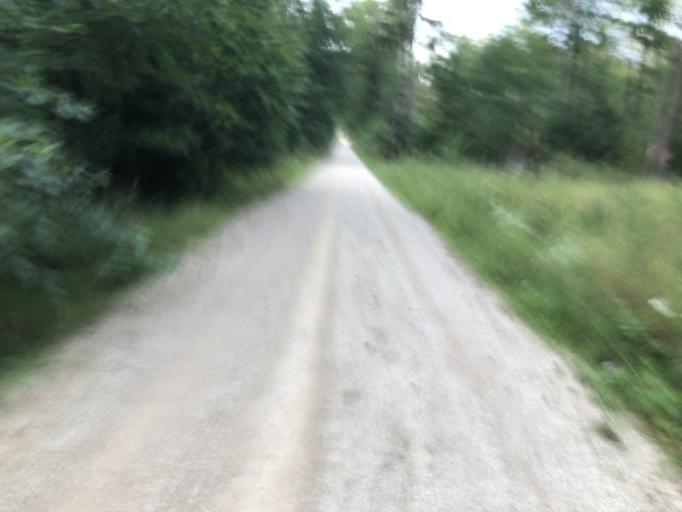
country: DE
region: Bavaria
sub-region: Regierungsbezirk Mittelfranken
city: Uttenreuth
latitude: 49.5725
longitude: 11.0760
